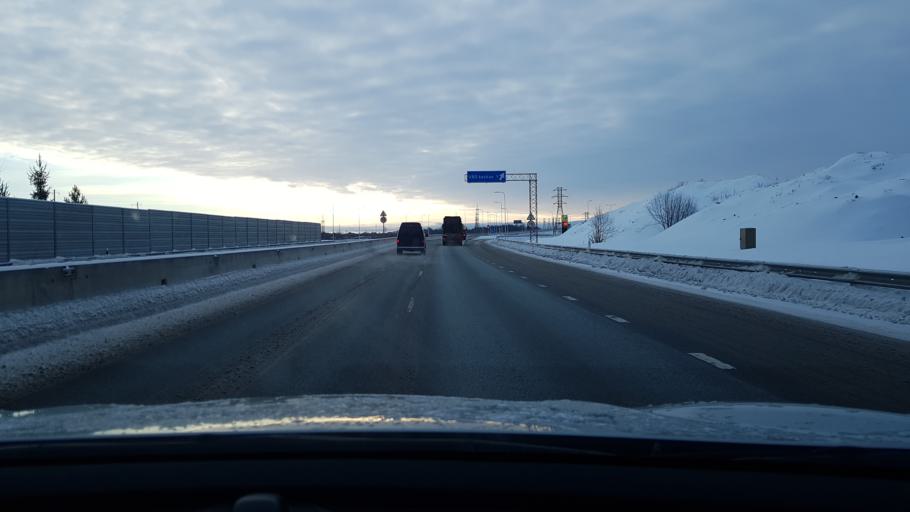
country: EE
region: Harju
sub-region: Joelaehtme vald
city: Loo
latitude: 59.4336
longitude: 24.9172
